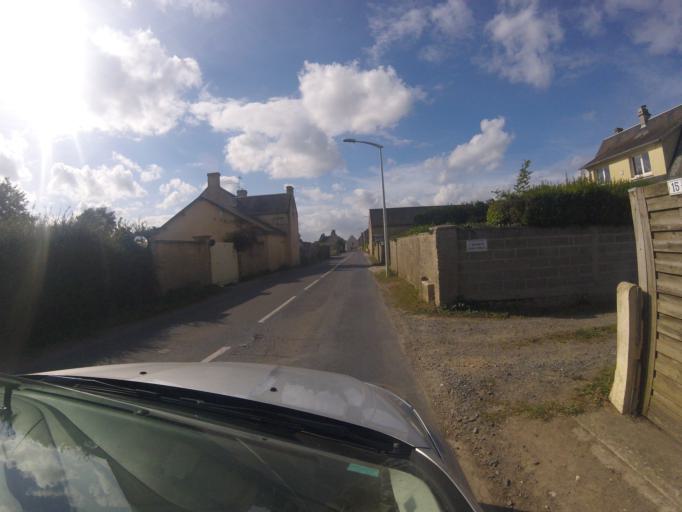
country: FR
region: Lower Normandy
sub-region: Departement du Calvados
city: Saint-Vigor-le-Grand
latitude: 49.3352
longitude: -0.6923
